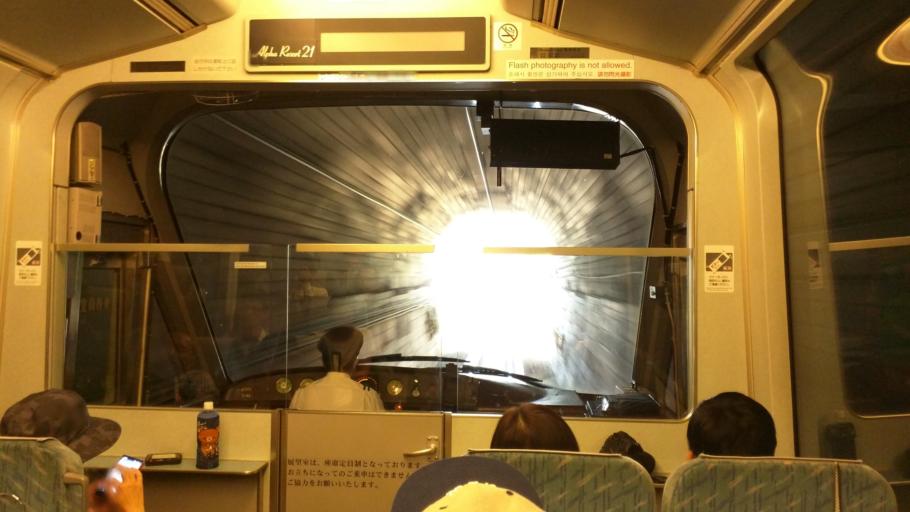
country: JP
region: Shizuoka
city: Ito
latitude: 34.9671
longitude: 139.0893
